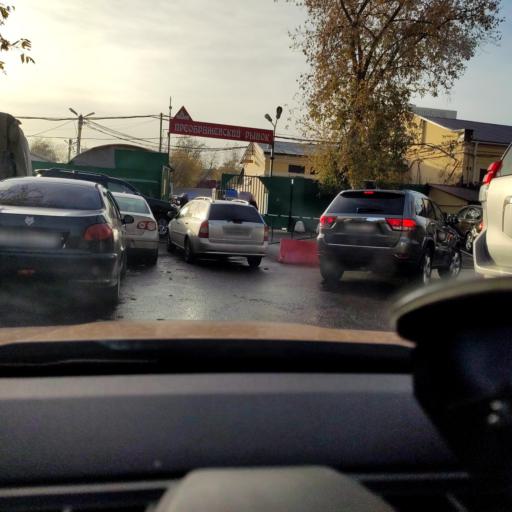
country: RU
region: Moskovskaya
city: Bogorodskoye
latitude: 55.7930
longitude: 37.7203
